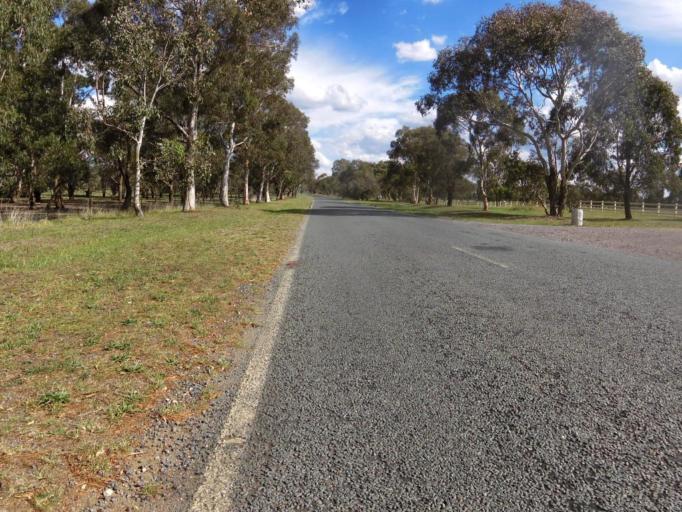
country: AU
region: Australian Capital Territory
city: Belconnen
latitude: -35.1757
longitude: 149.0715
